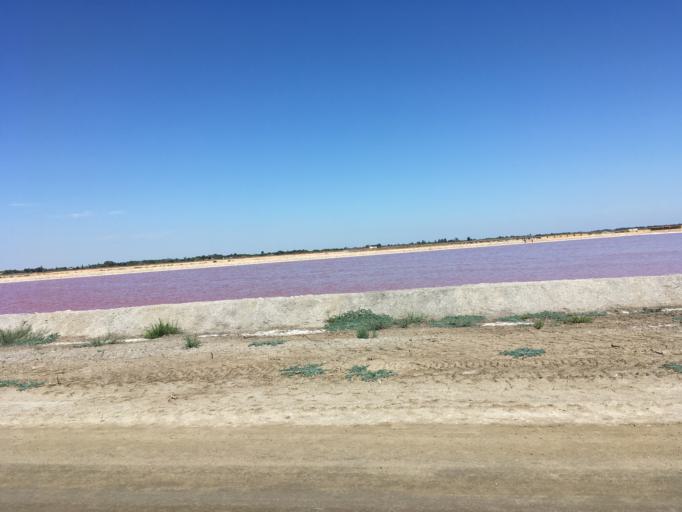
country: FR
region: Languedoc-Roussillon
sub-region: Departement du Gard
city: Aigues-Mortes
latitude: 43.5468
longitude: 4.1874
